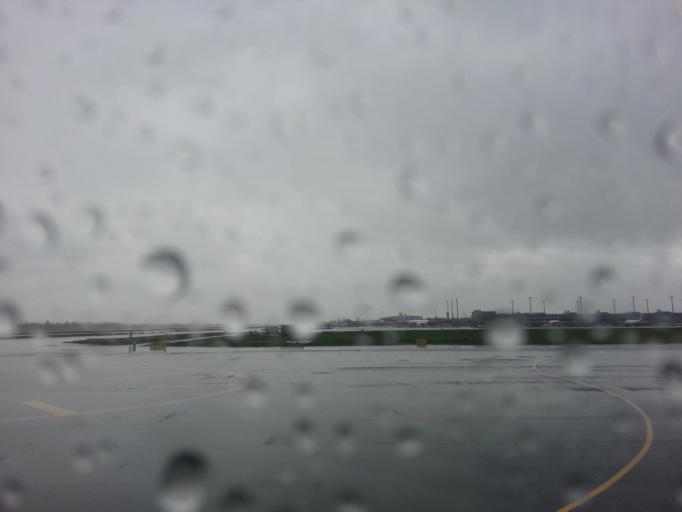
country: NO
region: Akershus
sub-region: Ullensaker
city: Jessheim
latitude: 60.1986
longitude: 11.1135
